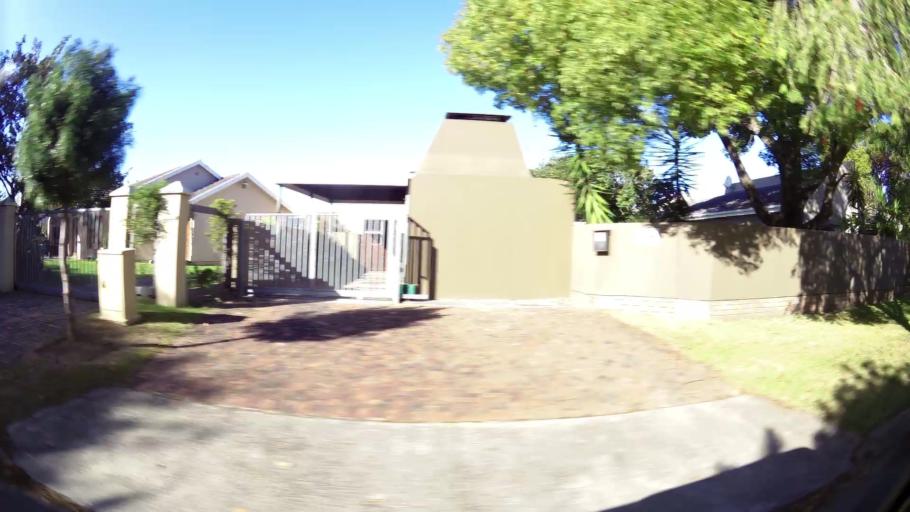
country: ZA
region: Western Cape
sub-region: Eden District Municipality
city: George
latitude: -33.9588
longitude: 22.4226
